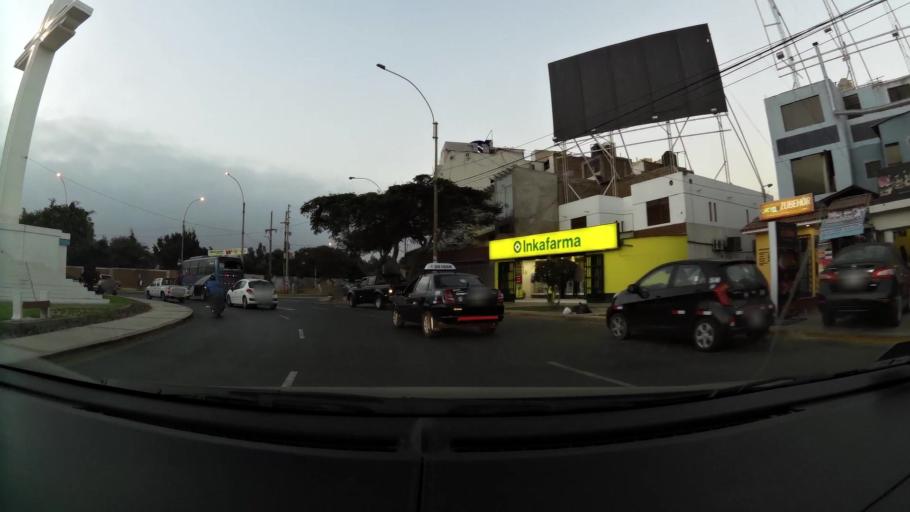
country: PE
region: La Libertad
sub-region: Provincia de Trujillo
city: Trujillo
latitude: -8.1197
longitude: -79.0402
